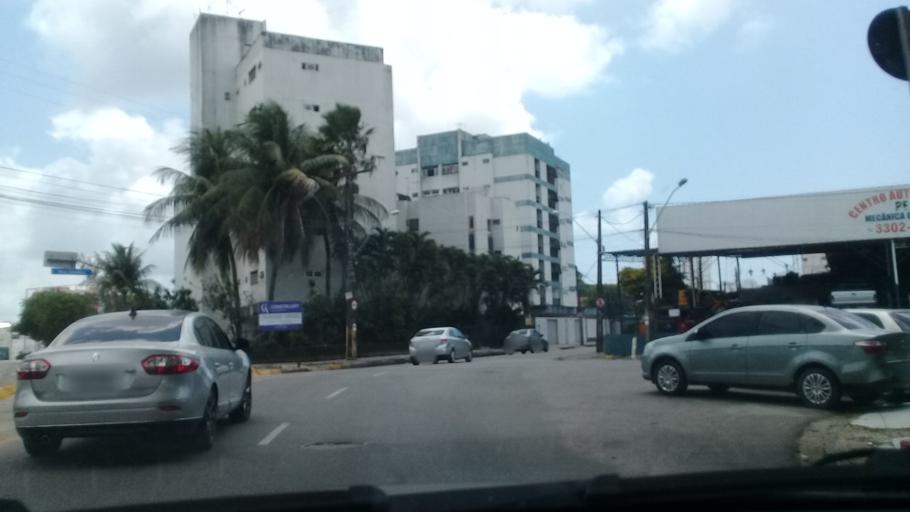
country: BR
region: Pernambuco
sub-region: Recife
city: Recife
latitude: -8.1072
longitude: -34.9151
